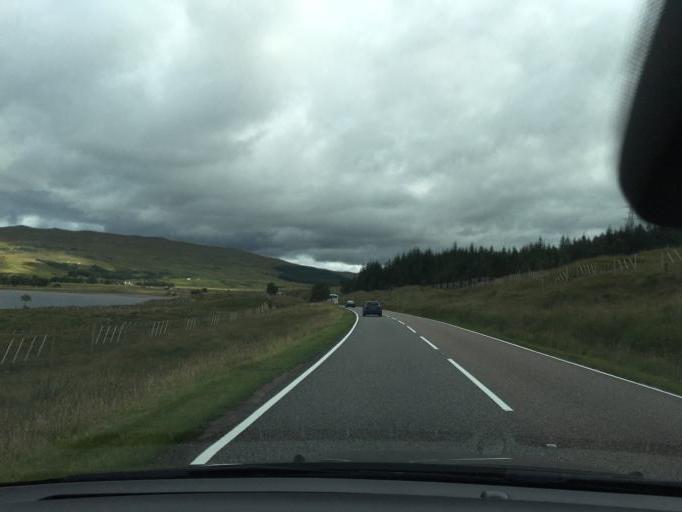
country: GB
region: Scotland
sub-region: Highland
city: Spean Bridge
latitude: 56.5507
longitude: -4.7526
